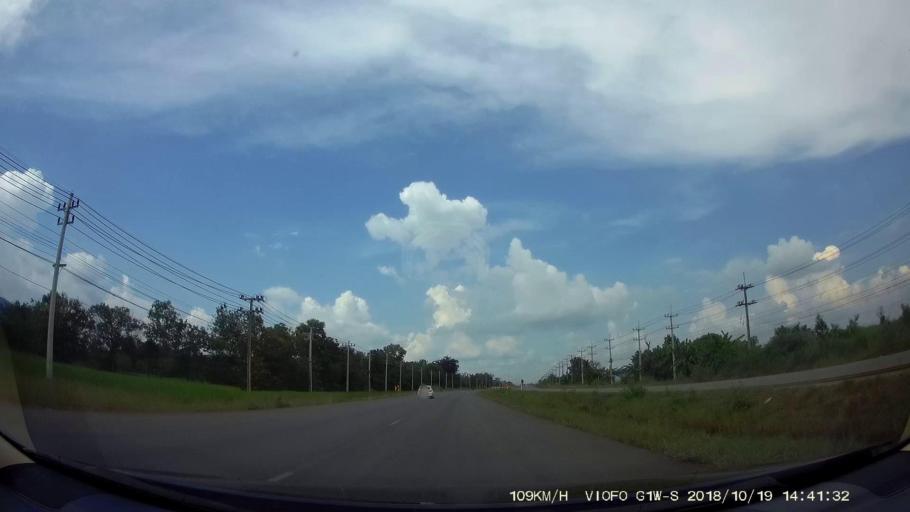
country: TH
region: Chaiyaphum
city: Phu Khiao
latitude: 16.2585
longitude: 102.1995
